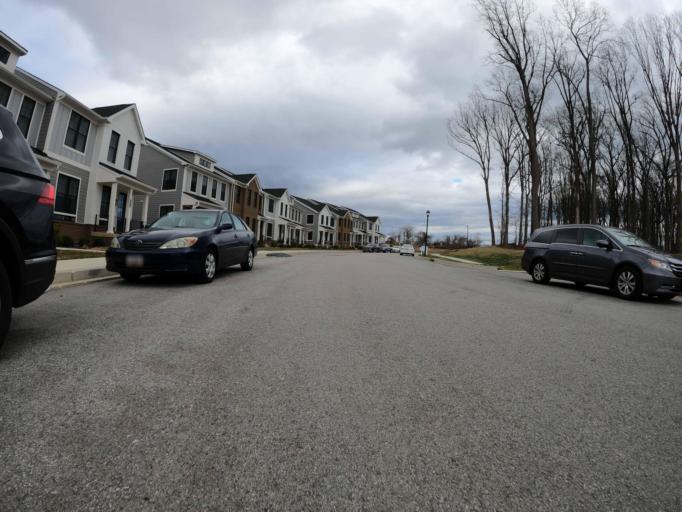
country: US
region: Maryland
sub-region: Howard County
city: Columbia
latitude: 39.2958
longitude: -76.8907
